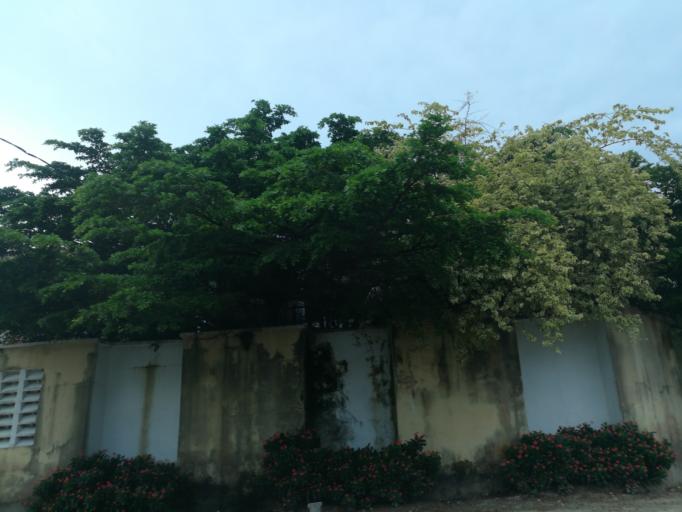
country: NG
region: Lagos
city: Ikoyi
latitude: 6.4459
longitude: 3.4729
